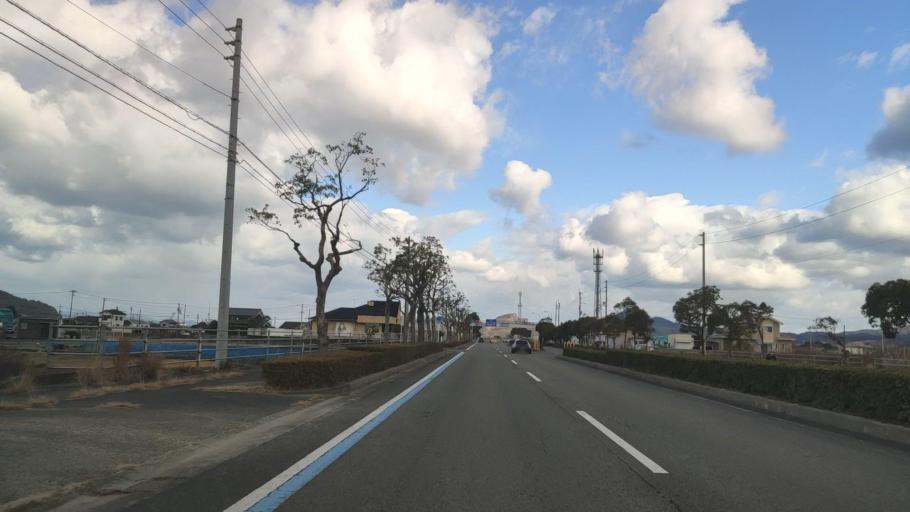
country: JP
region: Ehime
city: Hojo
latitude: 33.9515
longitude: 132.7746
